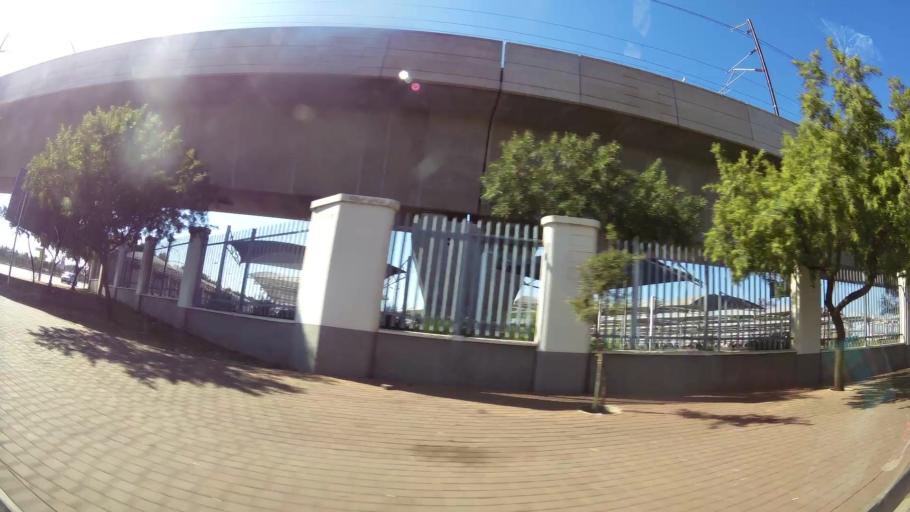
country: ZA
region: Gauteng
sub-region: City of Tshwane Metropolitan Municipality
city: Centurion
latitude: -25.8508
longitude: 28.1886
